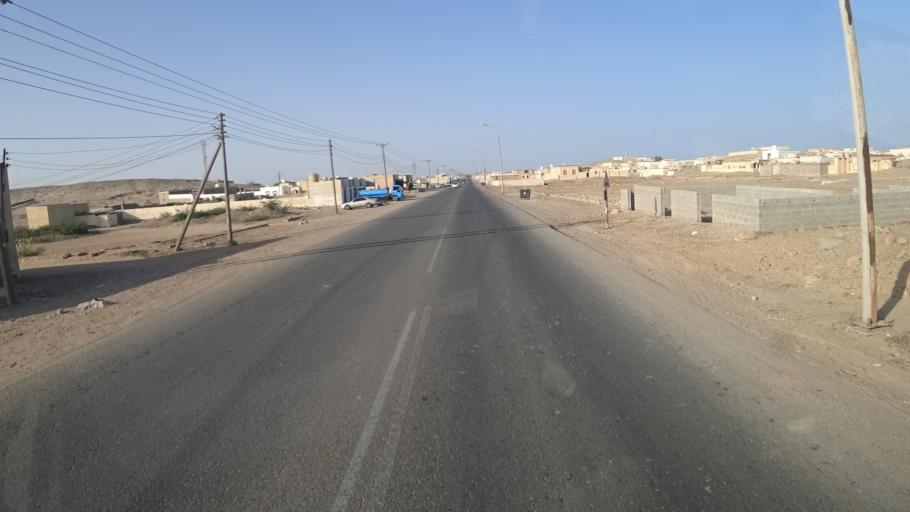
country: OM
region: Ash Sharqiyah
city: Sur
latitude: 22.1733
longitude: 59.7600
